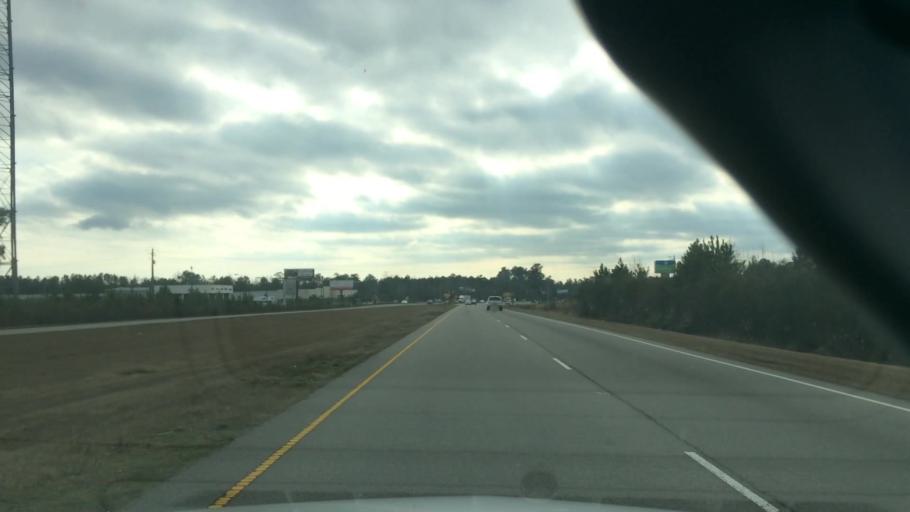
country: US
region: North Carolina
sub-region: Brunswick County
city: Shallotte
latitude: 33.9649
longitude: -78.4151
